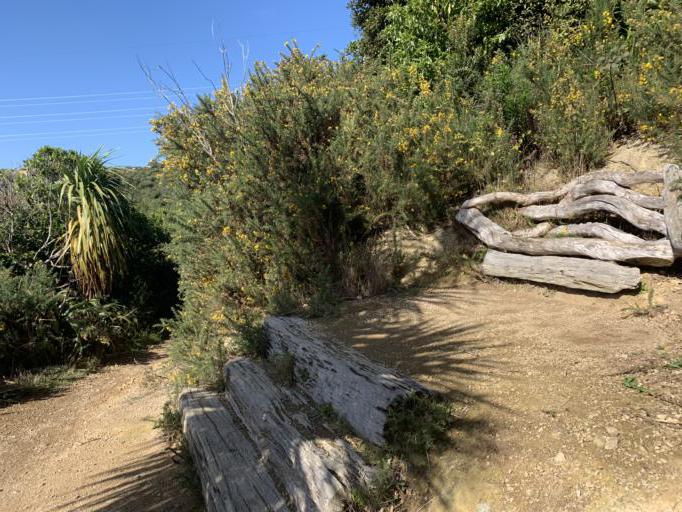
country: NZ
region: Wellington
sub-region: Wellington City
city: Brooklyn
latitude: -41.2992
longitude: 174.7537
